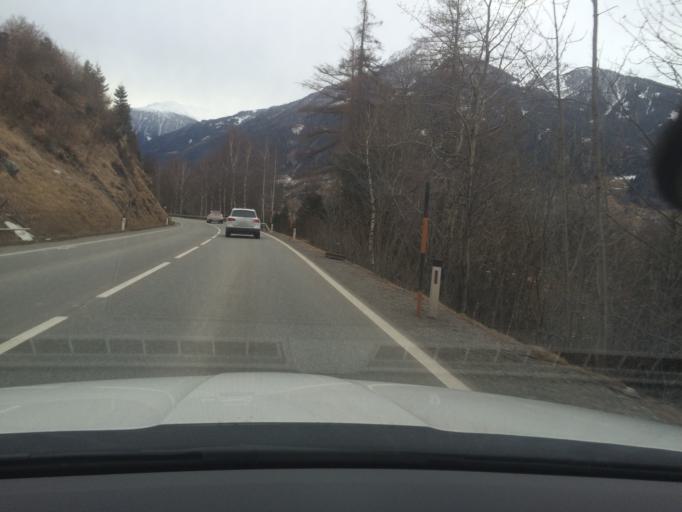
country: AT
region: Tyrol
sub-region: Politischer Bezirk Lienz
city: Matrei in Osttirol
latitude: 47.0094
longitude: 12.5398
